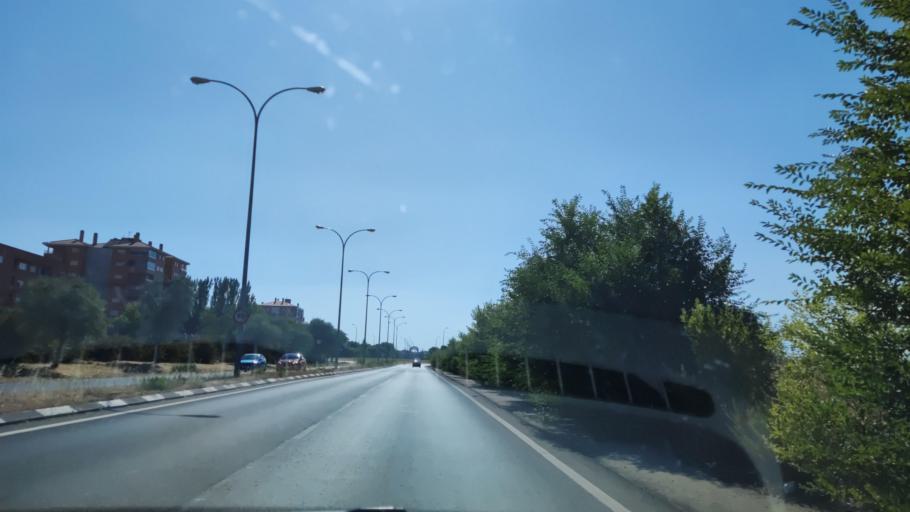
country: ES
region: Madrid
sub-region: Provincia de Madrid
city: Leganes
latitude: 40.3473
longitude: -3.7451
